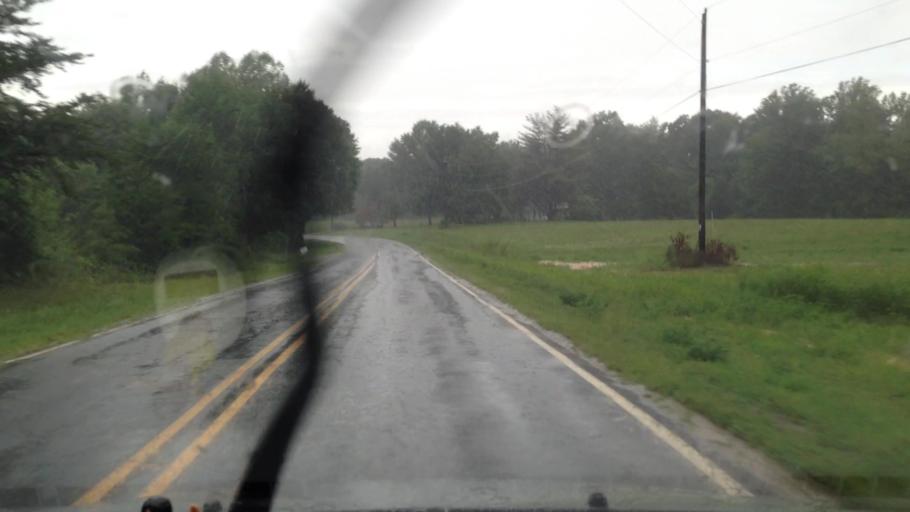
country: US
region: North Carolina
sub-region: Guilford County
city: Stokesdale
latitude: 36.2094
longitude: -80.0094
